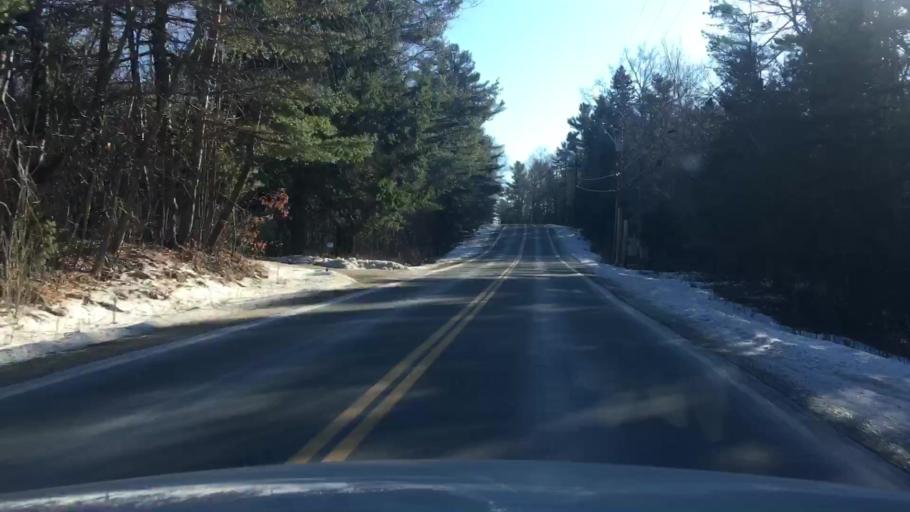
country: US
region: Maine
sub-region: Hancock County
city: Orland
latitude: 44.5381
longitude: -68.7462
